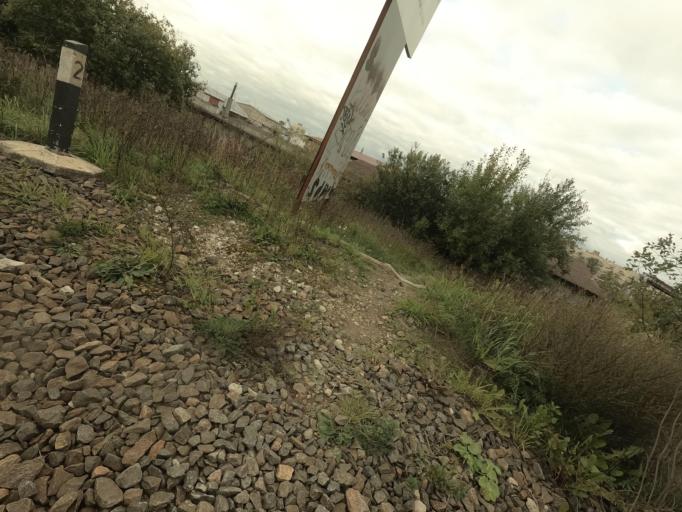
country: RU
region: Leningrad
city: Rybatskoye
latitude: 59.8350
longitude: 30.4857
